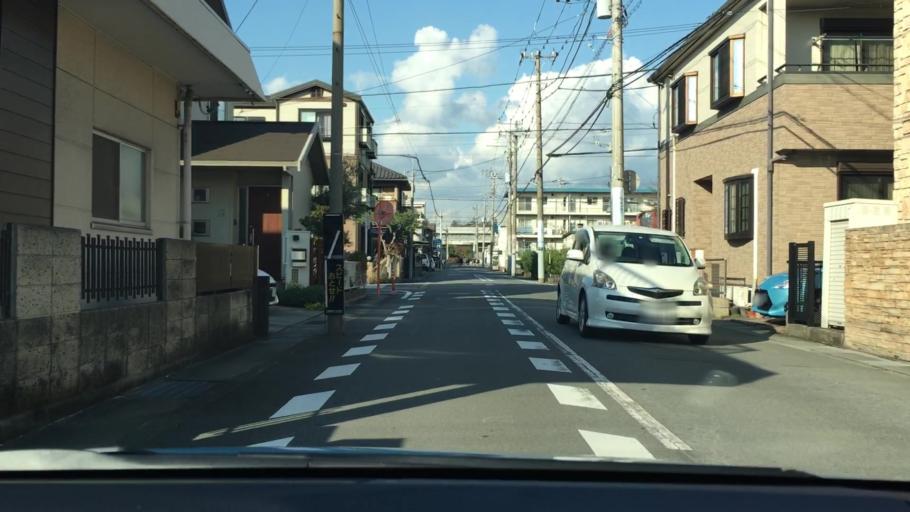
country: JP
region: Shizuoka
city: Numazu
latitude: 35.1216
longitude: 138.8741
